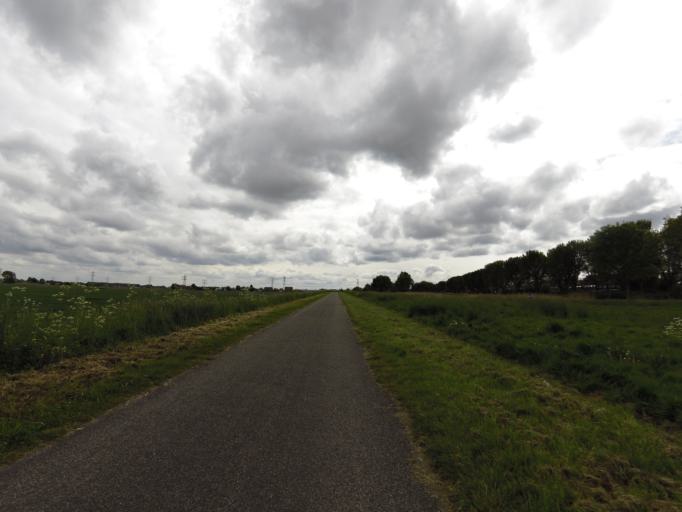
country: NL
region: South Holland
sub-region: Gemeente Brielle
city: Brielle
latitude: 51.8928
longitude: 4.1718
